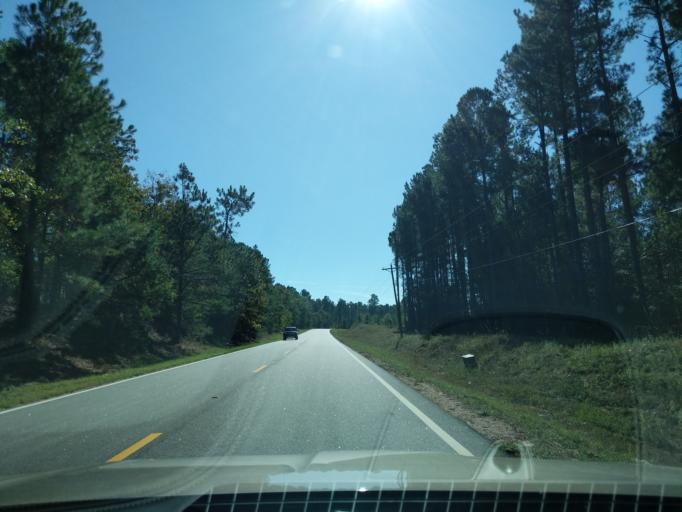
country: US
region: Georgia
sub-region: Richmond County
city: Hephzibah
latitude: 33.2811
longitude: -82.0173
